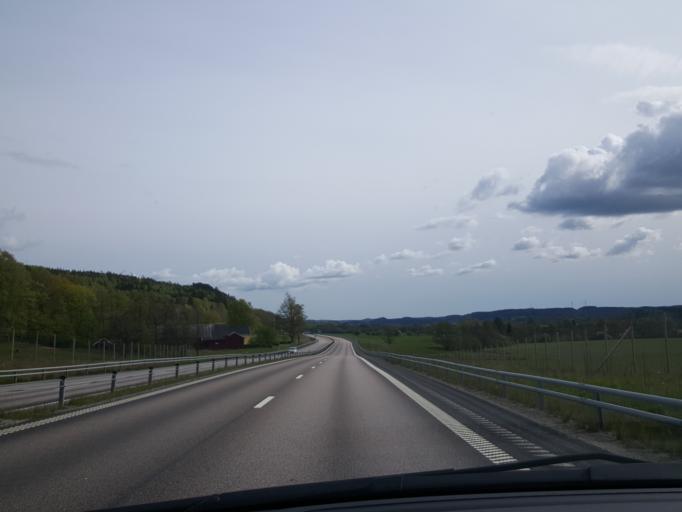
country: SE
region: Vaestra Goetaland
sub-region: Lilla Edets Kommun
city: Lilla Edet
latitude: 58.1671
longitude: 12.1378
